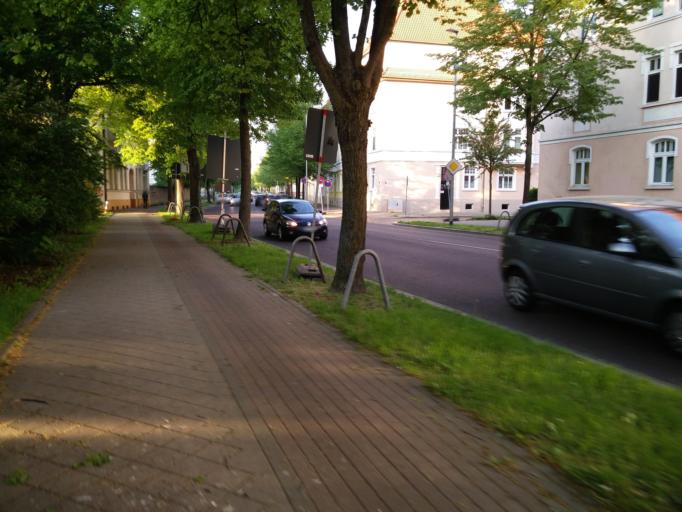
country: DE
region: Saxony-Anhalt
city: Magdeburg
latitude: 52.1079
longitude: 11.6277
